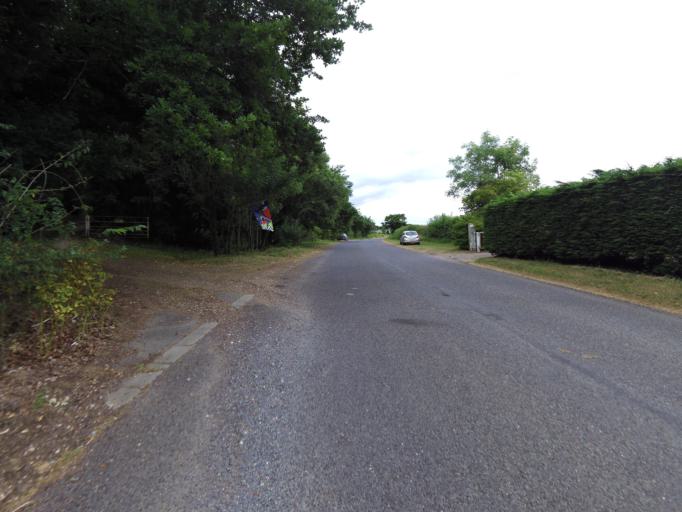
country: GB
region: England
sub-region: Norfolk
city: Harleston
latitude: 52.4242
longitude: 1.3549
